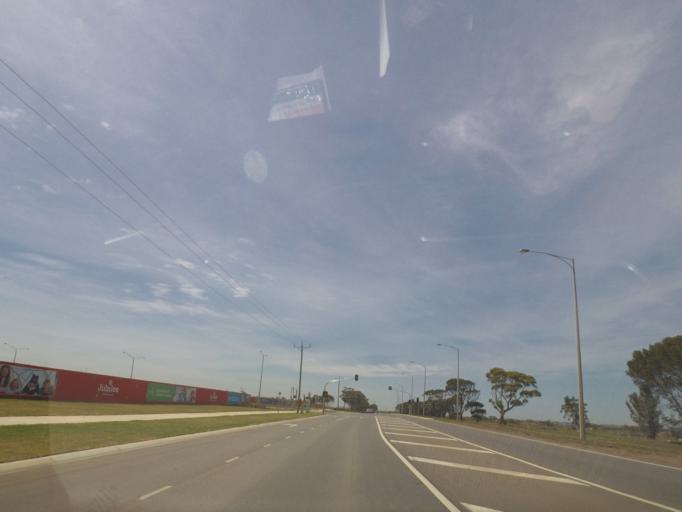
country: AU
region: Victoria
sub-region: Wyndham
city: Wyndham Vale
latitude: -37.8555
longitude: 144.5897
